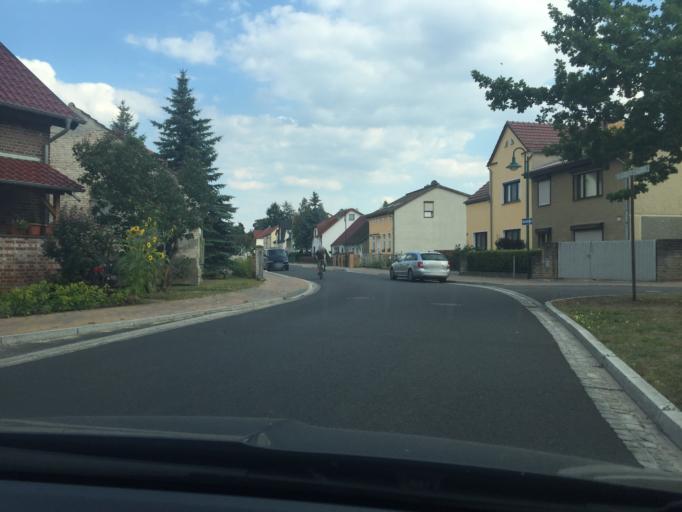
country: DE
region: Brandenburg
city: Erkner
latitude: 52.3874
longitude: 13.7460
